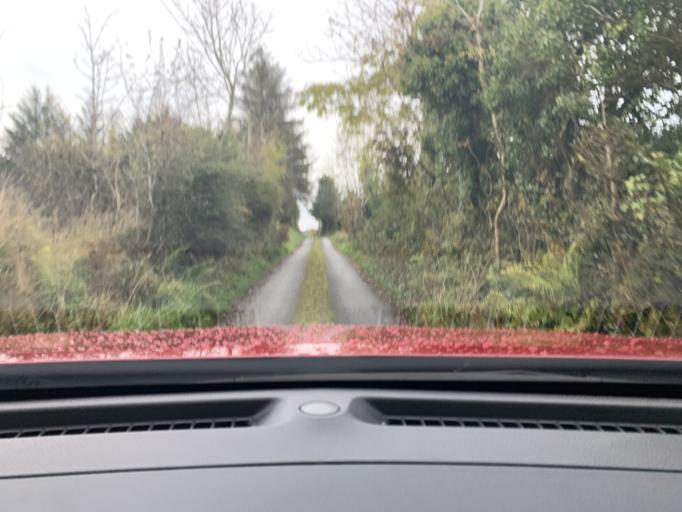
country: IE
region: Connaught
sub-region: Roscommon
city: Ballaghaderreen
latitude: 53.9172
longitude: -8.5669
